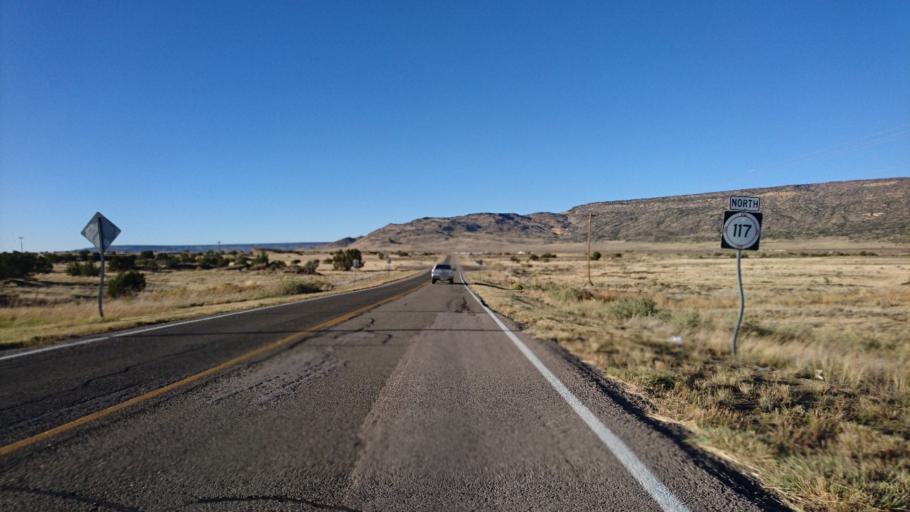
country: US
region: New Mexico
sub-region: Cibola County
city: Grants
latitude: 35.0872
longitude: -107.7696
